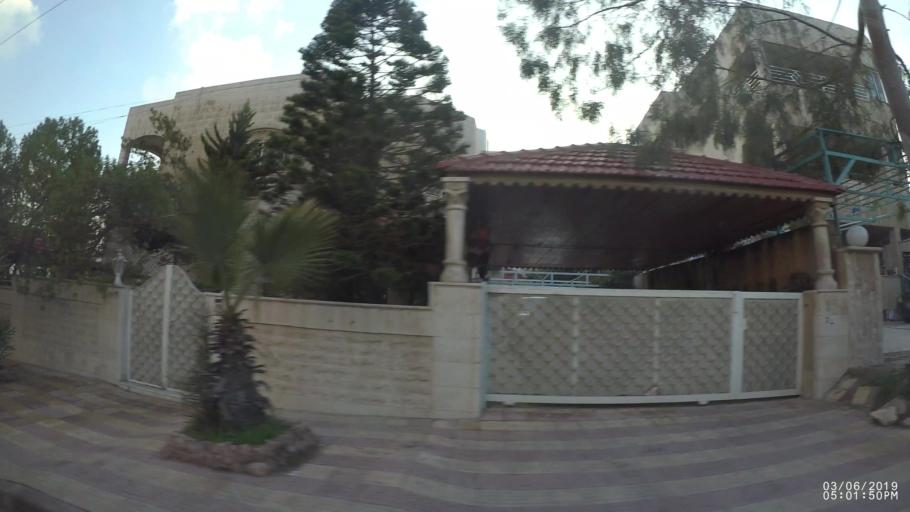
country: JO
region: Amman
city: Amman
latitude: 31.9967
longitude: 35.9520
